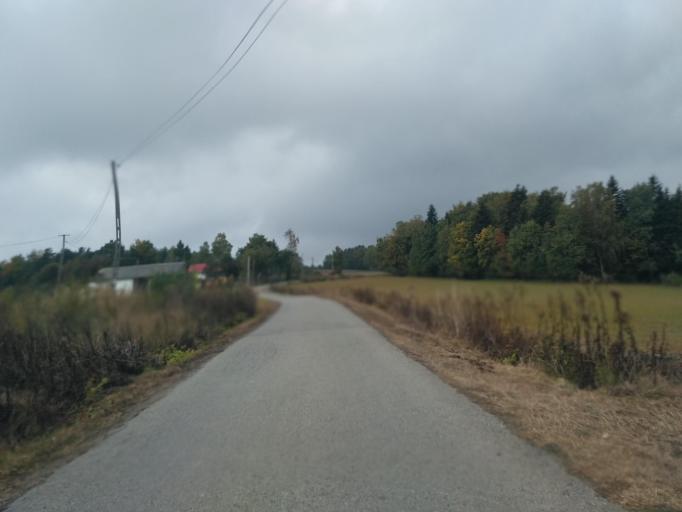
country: PL
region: Subcarpathian Voivodeship
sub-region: Powiat debicki
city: Brzostek
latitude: 49.9450
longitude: 21.4483
